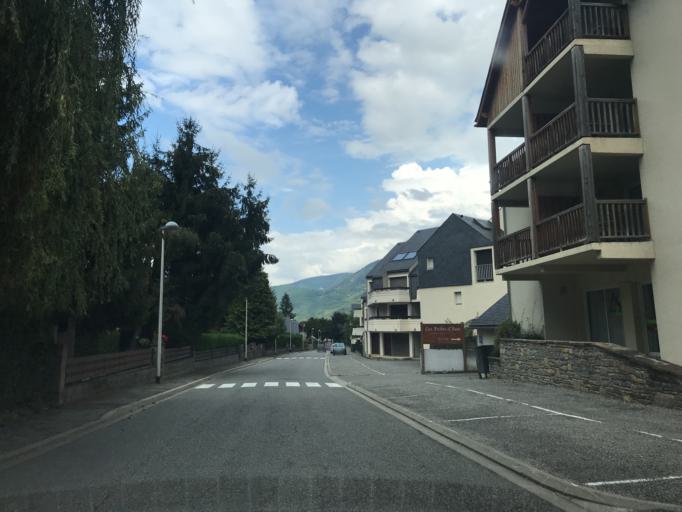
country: FR
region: Midi-Pyrenees
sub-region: Departement des Hautes-Pyrenees
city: Saint-Lary-Soulan
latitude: 42.8197
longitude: 0.3237
